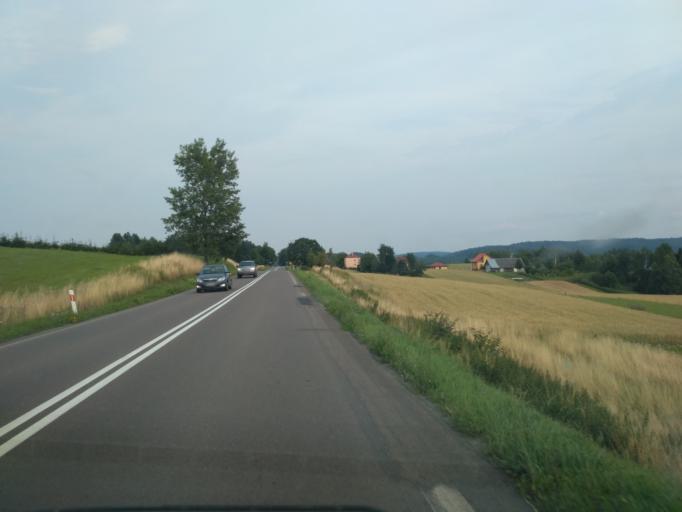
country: PL
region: Subcarpathian Voivodeship
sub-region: Powiat przemyski
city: Przedmiescie Dubieckie
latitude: 49.8267
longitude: 22.3158
